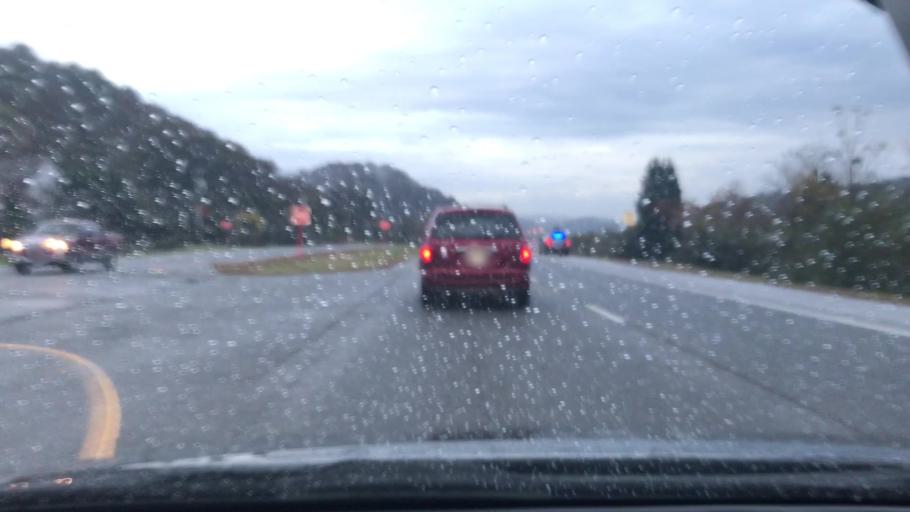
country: US
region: Tennessee
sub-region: Cheatham County
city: Ashland City
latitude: 36.2563
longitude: -87.0403
